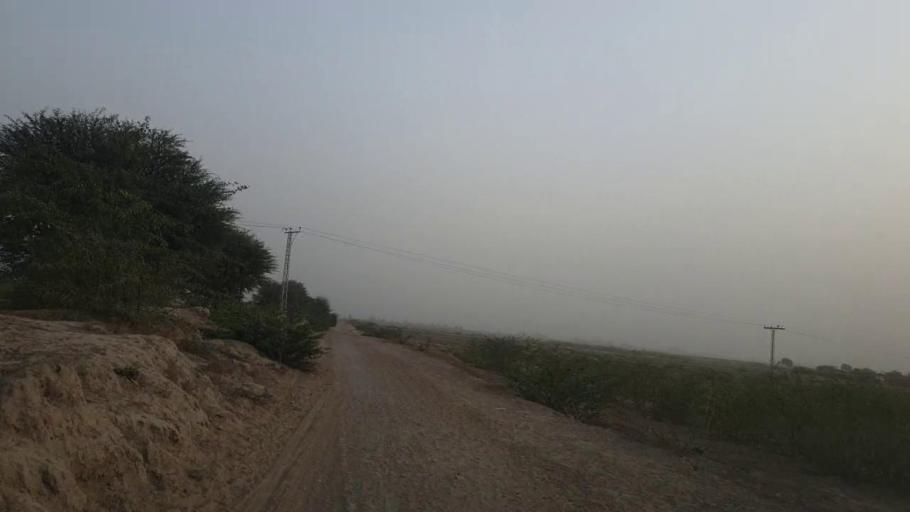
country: PK
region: Sindh
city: Kunri
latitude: 25.1144
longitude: 69.5524
